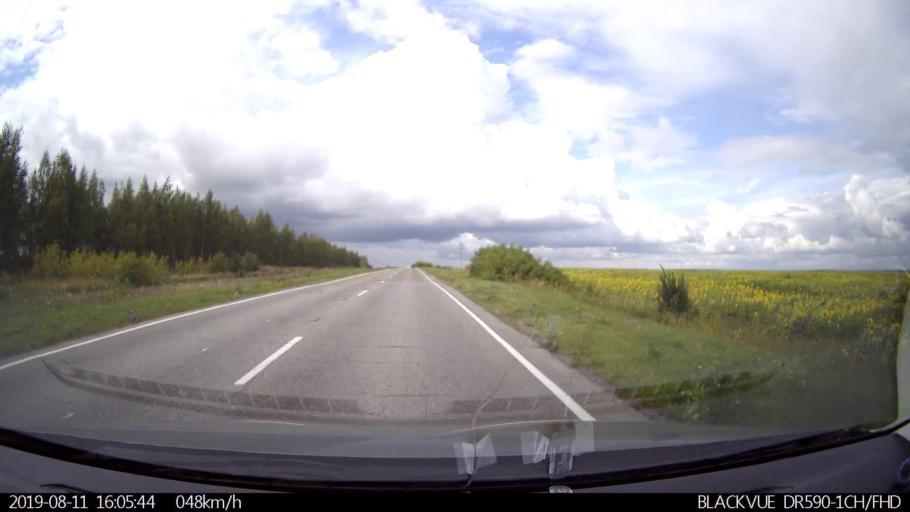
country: RU
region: Ulyanovsk
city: Ignatovka
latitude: 53.9629
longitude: 47.6491
